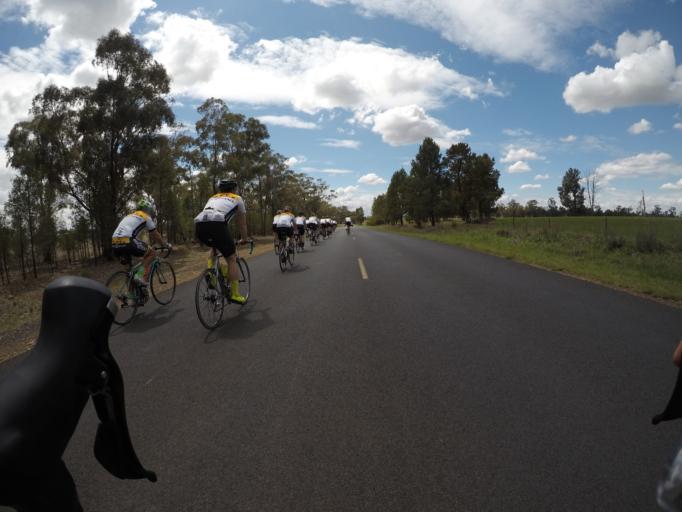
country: AU
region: New South Wales
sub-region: Dubbo Municipality
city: Dubbo
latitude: -32.3013
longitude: 148.5973
